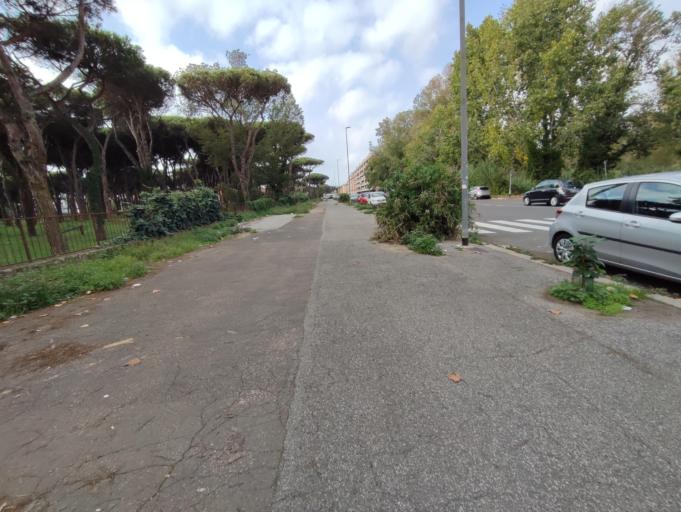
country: IT
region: Latium
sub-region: Citta metropolitana di Roma Capitale
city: Lido di Ostia
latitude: 41.7333
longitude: 12.2991
